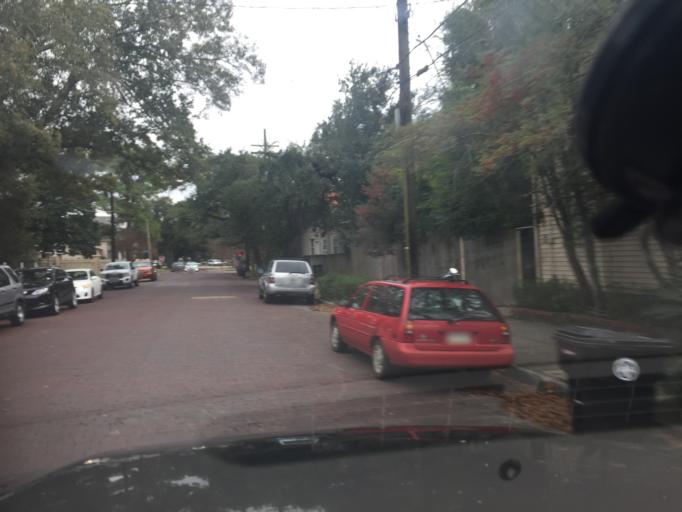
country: US
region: Louisiana
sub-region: Orleans Parish
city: New Orleans
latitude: 29.9745
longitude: -90.0752
